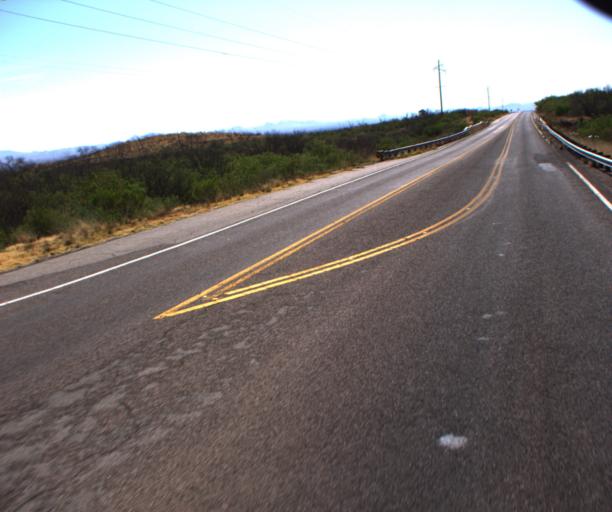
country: US
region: Arizona
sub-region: Cochise County
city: Bisbee
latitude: 31.4424
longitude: -109.8264
